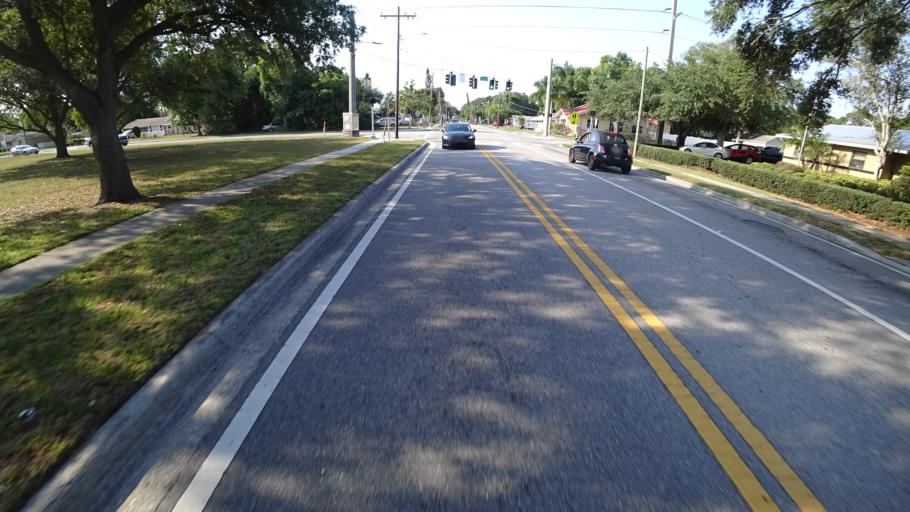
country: US
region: Florida
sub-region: Manatee County
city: West Bradenton
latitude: 27.4925
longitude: -82.6039
